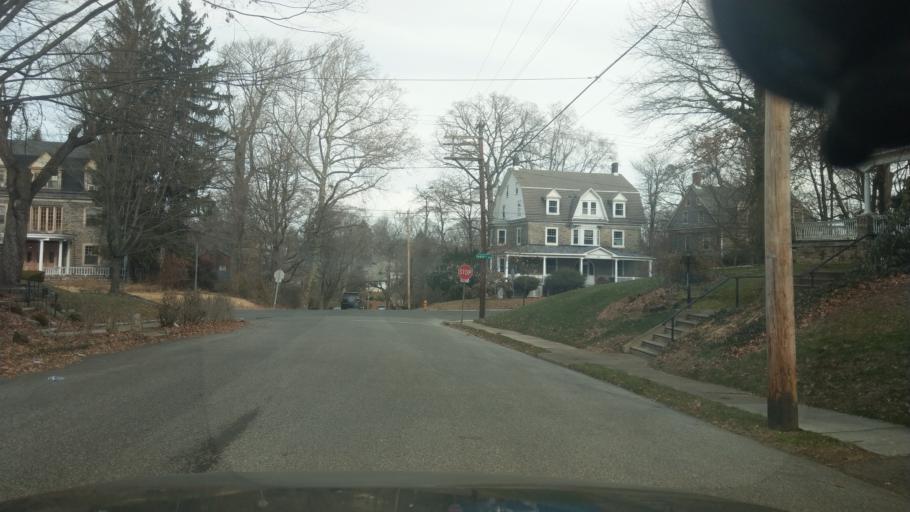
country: US
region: Pennsylvania
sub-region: Montgomery County
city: Jenkintown
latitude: 40.0568
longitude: -75.1344
